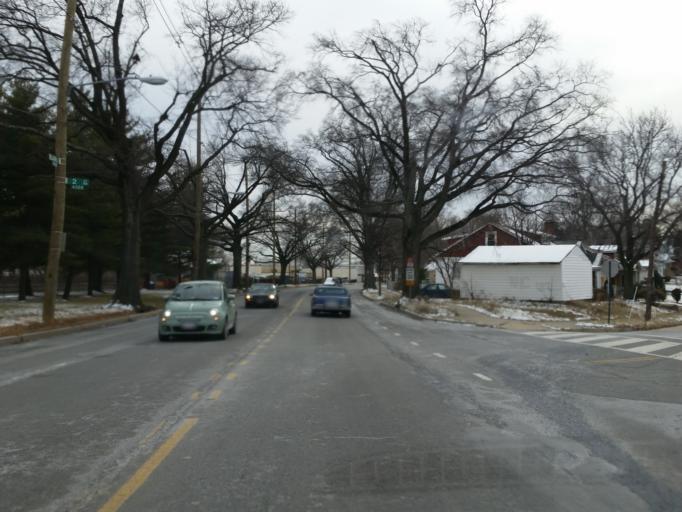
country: US
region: Maryland
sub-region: Montgomery County
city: Takoma Park
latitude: 38.9673
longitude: -77.0137
